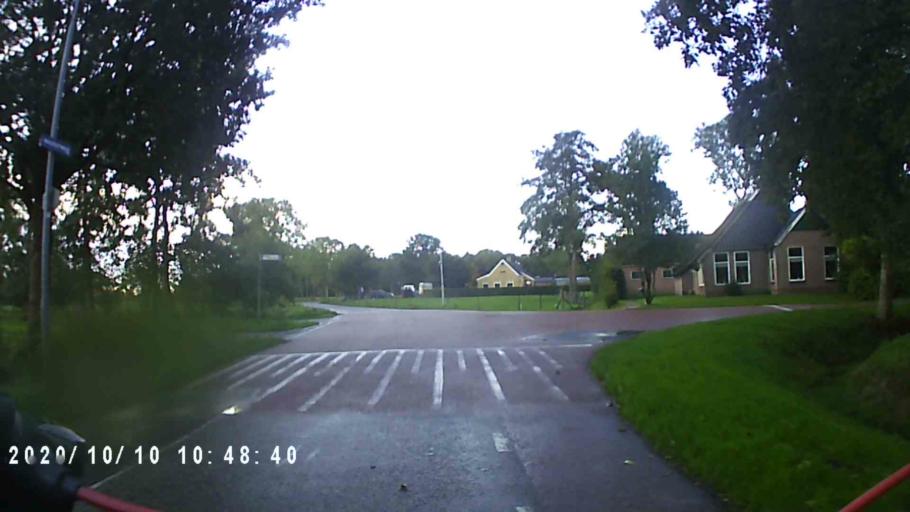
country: NL
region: Groningen
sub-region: Gemeente Grootegast
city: Grootegast
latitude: 53.1635
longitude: 6.2416
